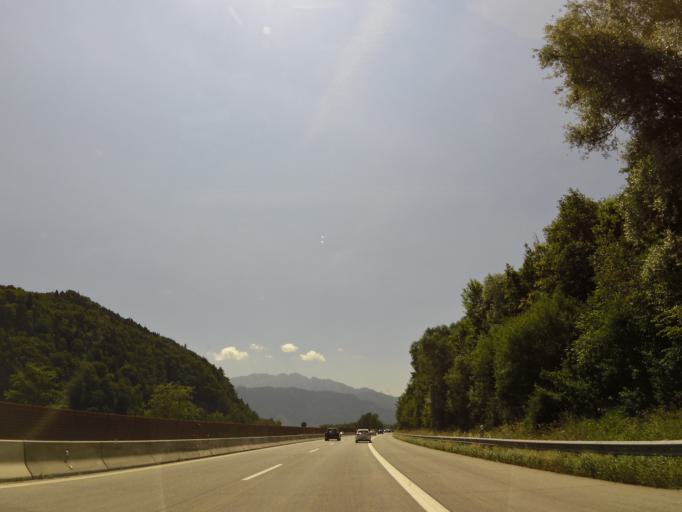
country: AT
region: Tyrol
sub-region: Politischer Bezirk Kufstein
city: Erl
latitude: 47.6656
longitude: 12.1823
